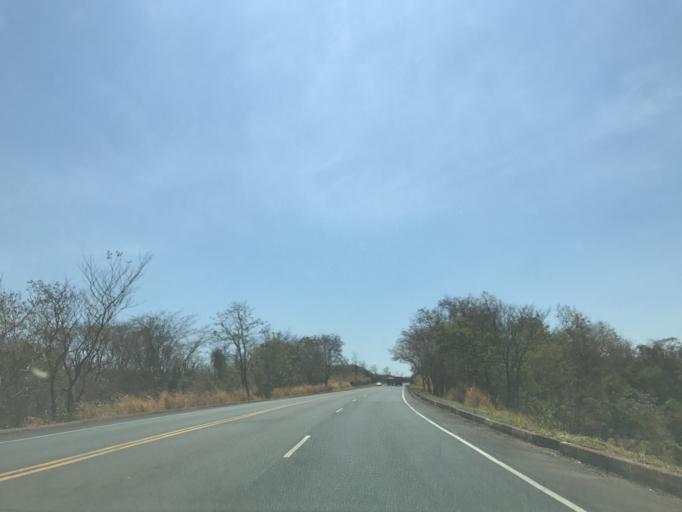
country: BR
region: Minas Gerais
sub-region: Frutal
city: Frutal
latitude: -19.8721
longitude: -48.9736
